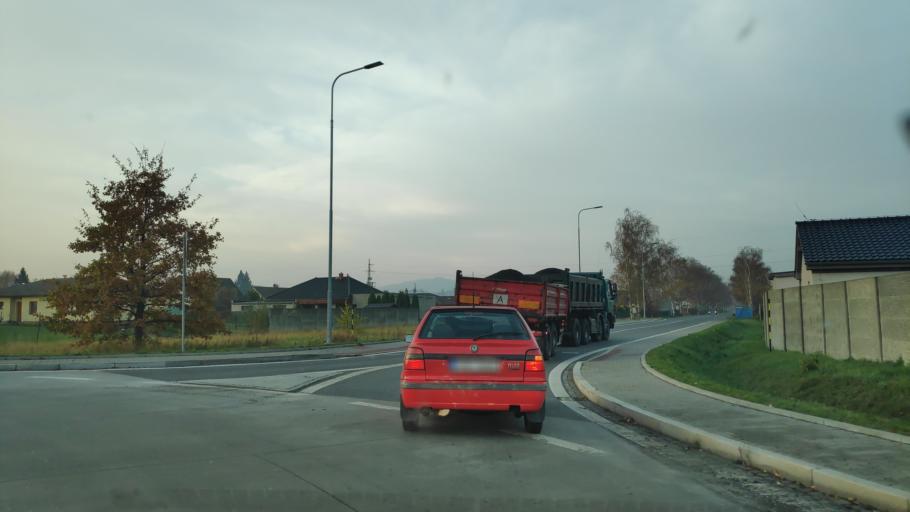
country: CZ
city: Sviadnov
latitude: 49.6951
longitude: 18.3209
